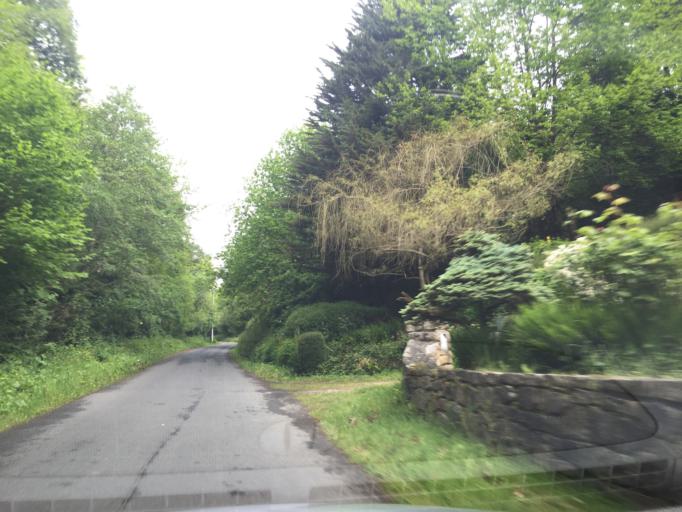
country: FR
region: Brittany
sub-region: Departement des Cotes-d'Armor
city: Saint-Cast-le-Guildo
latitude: 48.5942
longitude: -2.2290
